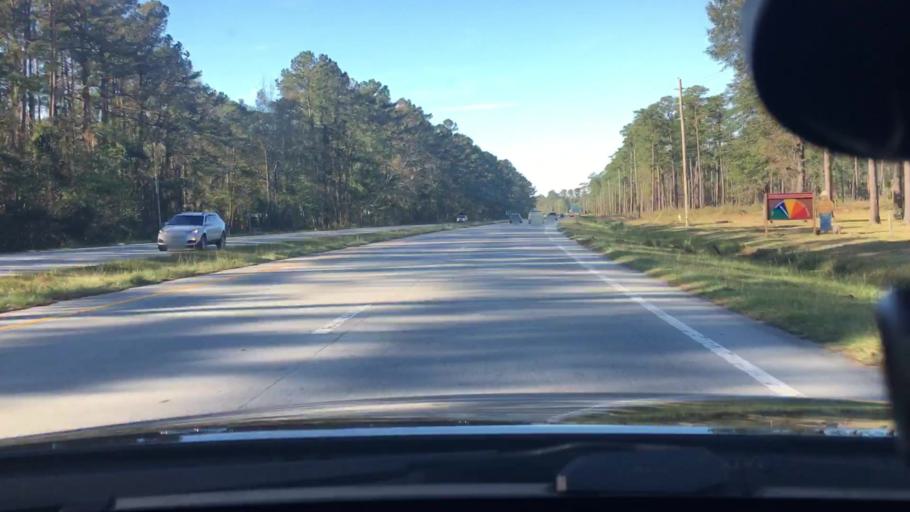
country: US
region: North Carolina
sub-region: Craven County
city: Neuse Forest
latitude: 34.9897
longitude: -76.9823
